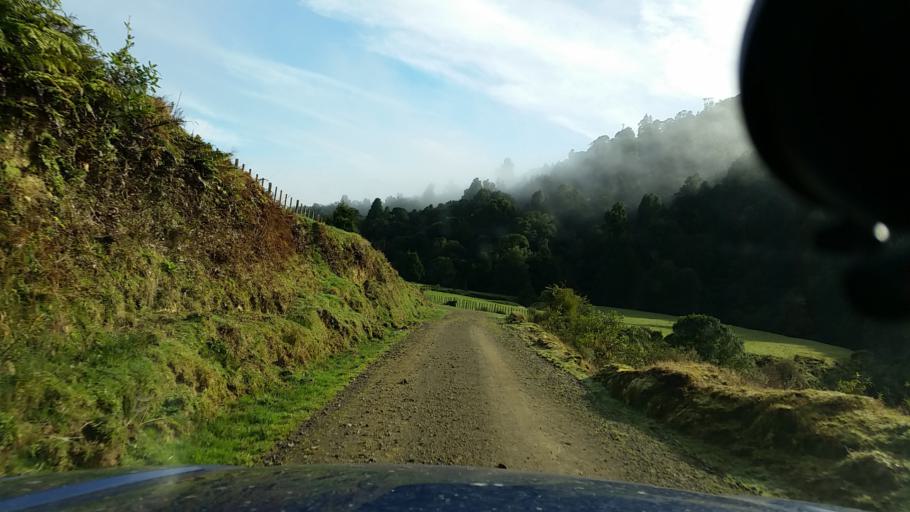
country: NZ
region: Taranaki
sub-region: New Plymouth District
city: Waitara
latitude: -38.9780
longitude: 174.7483
